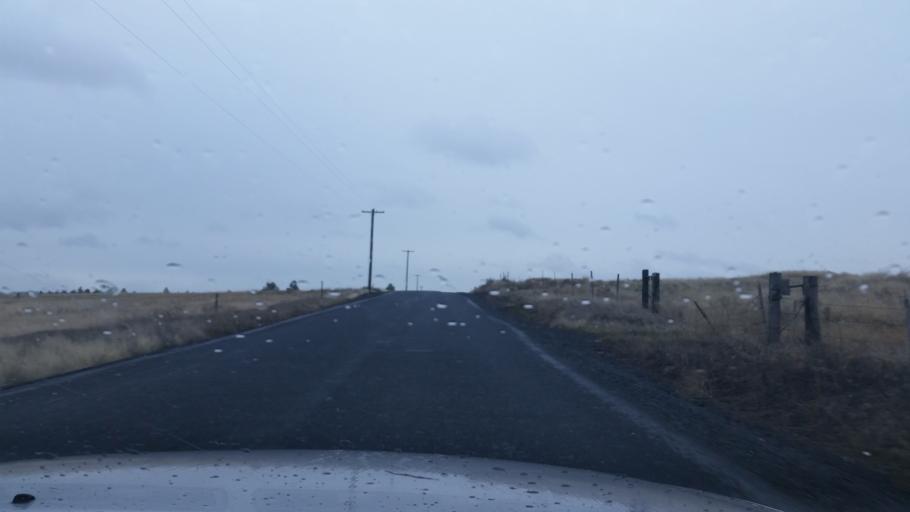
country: US
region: Washington
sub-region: Spokane County
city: Medical Lake
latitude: 47.6145
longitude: -117.7759
